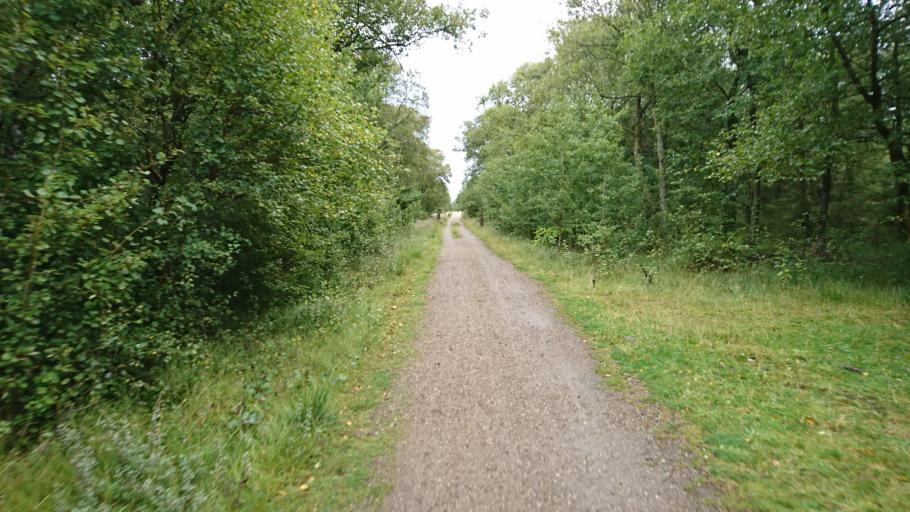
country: DK
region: South Denmark
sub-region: Fano Kommune
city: Nordby
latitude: 55.3815
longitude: 8.4270
